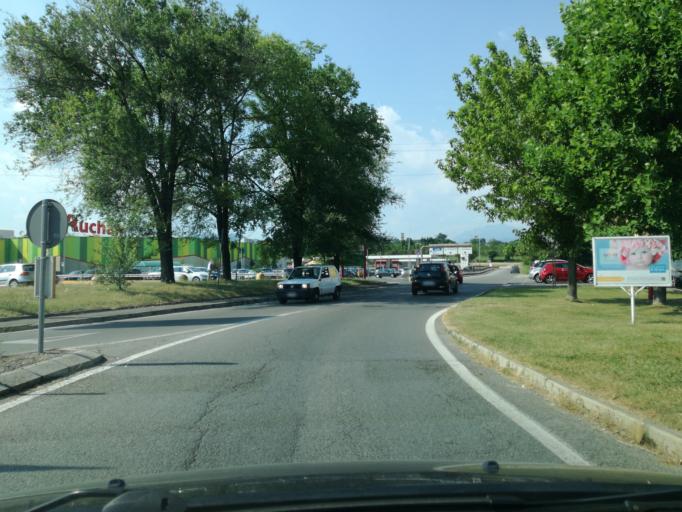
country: IT
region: Lombardy
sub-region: Provincia di Lecco
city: Merate
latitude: 45.6886
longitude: 9.4213
